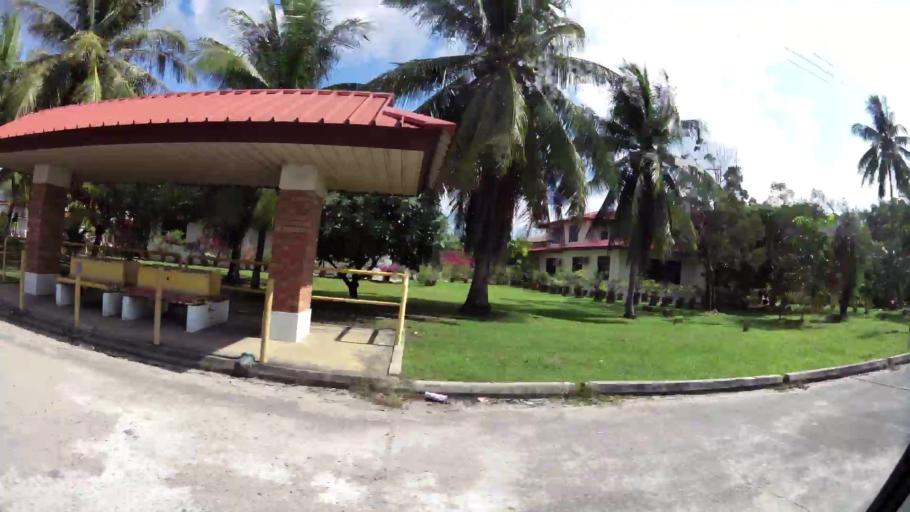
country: BN
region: Brunei and Muara
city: Bandar Seri Begawan
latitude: 4.9629
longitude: 114.9537
